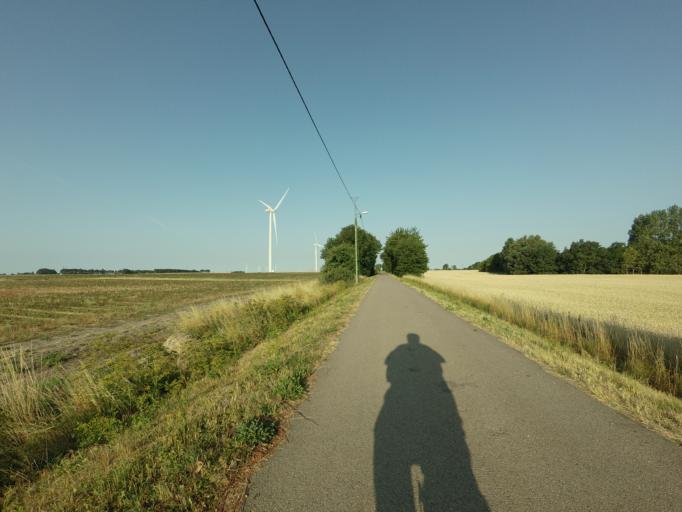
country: SE
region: Skane
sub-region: Landskrona
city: Asmundtorp
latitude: 55.8800
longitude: 12.9158
